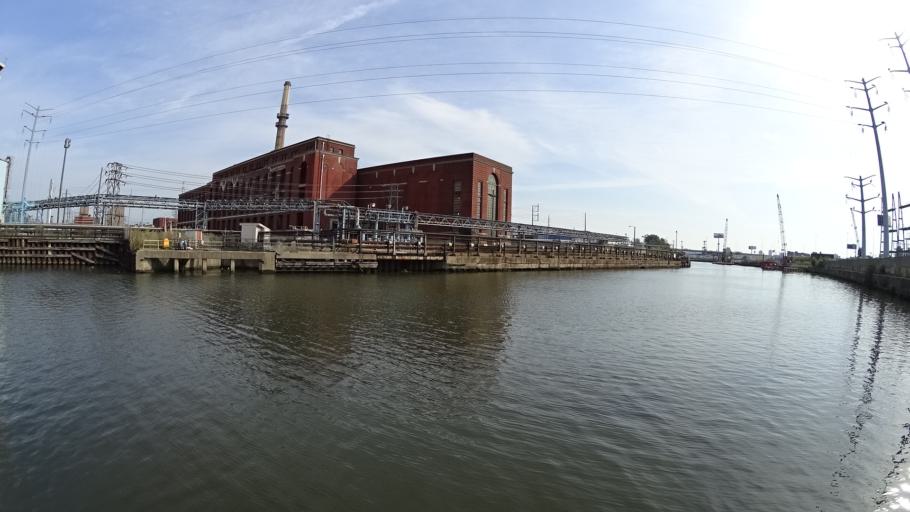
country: US
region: Illinois
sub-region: Cook County
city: Chicago
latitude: 41.8471
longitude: -87.6543
